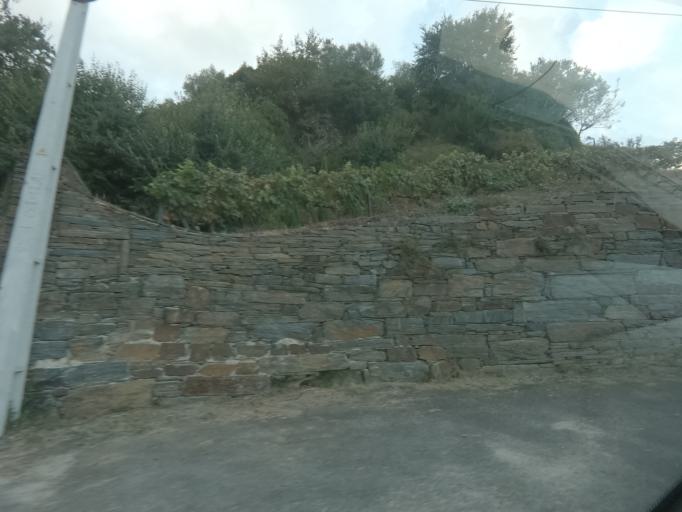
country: PT
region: Vila Real
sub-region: Mesao Frio
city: Mesao Frio
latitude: 41.1712
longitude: -7.8755
